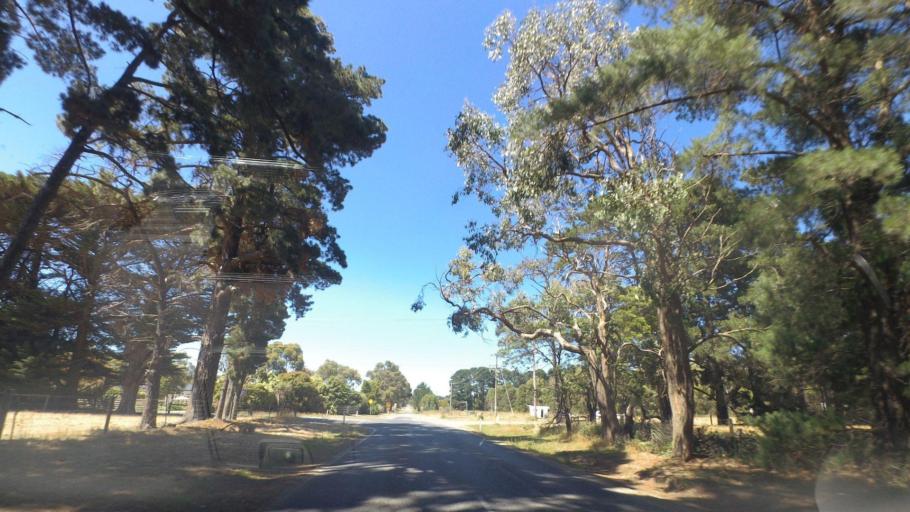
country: AU
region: Victoria
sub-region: Mornington Peninsula
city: Hastings
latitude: -38.2996
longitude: 145.1272
